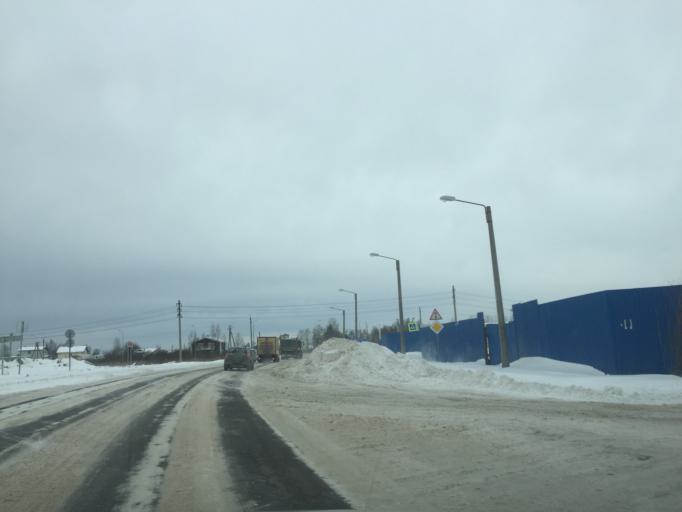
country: RU
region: Leningrad
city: Imeni Sverdlova
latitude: 59.7982
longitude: 30.6672
